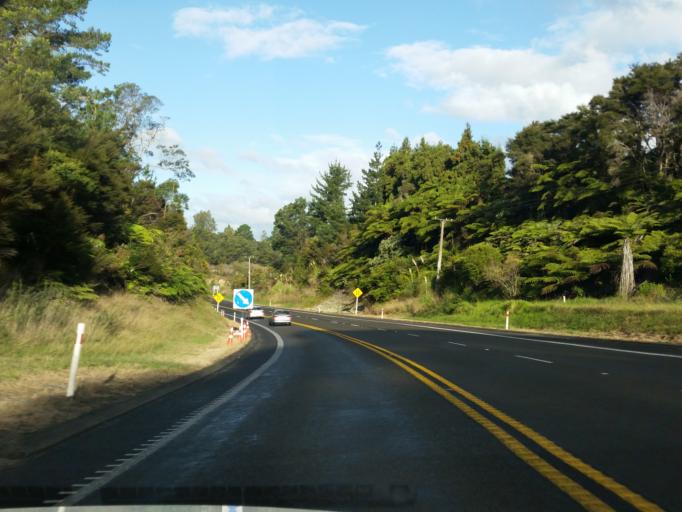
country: NZ
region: Bay of Plenty
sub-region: Western Bay of Plenty District
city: Katikati
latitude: -37.6326
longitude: 175.9574
